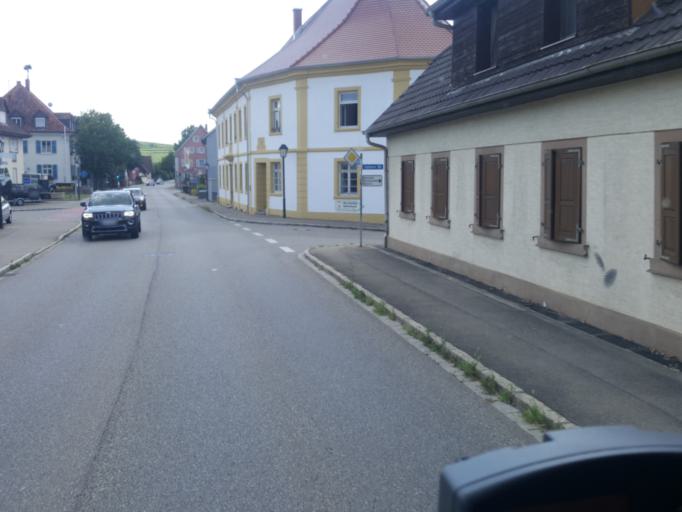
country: DE
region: Baden-Wuerttemberg
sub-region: Freiburg Region
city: Buggingen
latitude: 47.8308
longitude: 7.6209
